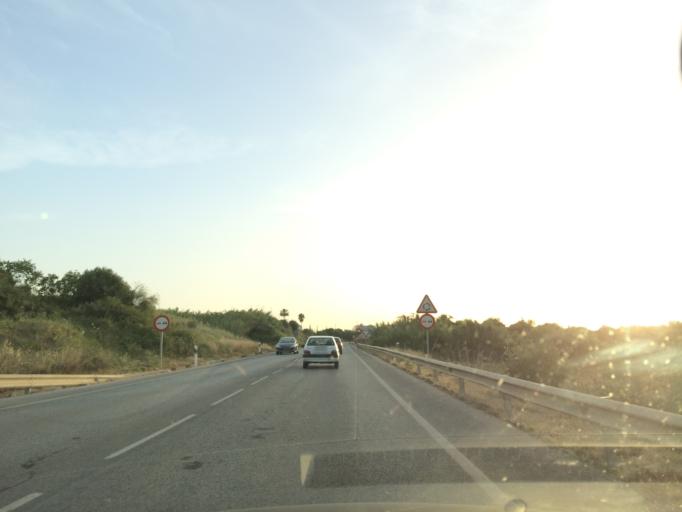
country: ES
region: Andalusia
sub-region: Provincia de Malaga
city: Alhaurin de la Torre
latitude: 36.6688
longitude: -4.5723
